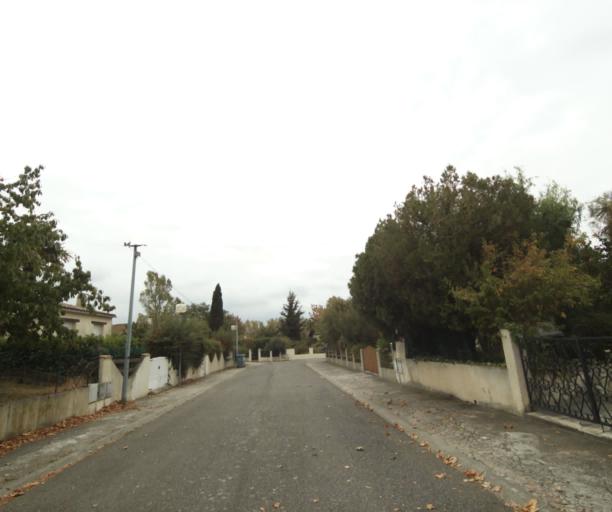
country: FR
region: Midi-Pyrenees
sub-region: Departement de la Haute-Garonne
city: Villefranche-de-Lauragais
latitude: 43.3971
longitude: 1.7236
